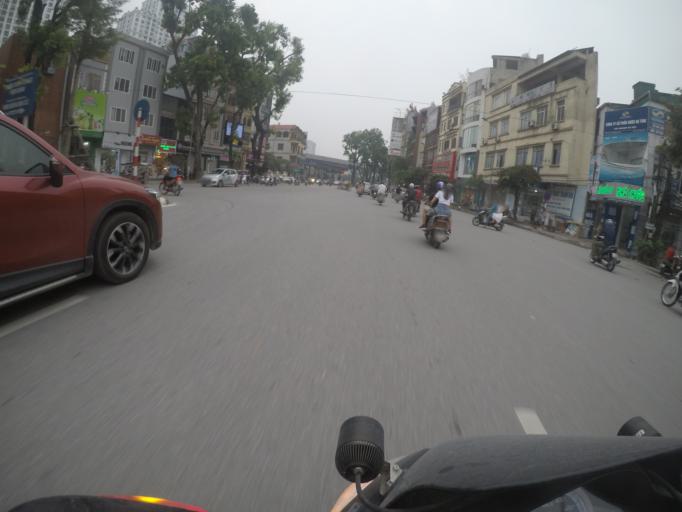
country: VN
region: Ha Noi
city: Dong Da
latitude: 21.0044
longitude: 105.8181
